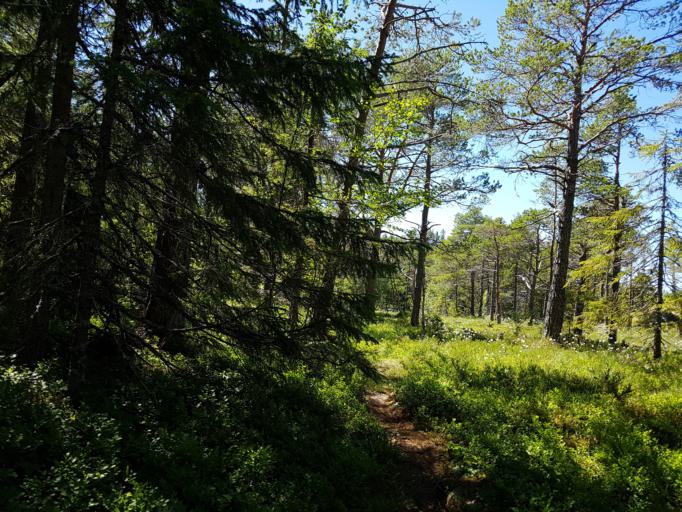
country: NO
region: Sor-Trondelag
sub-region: Melhus
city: Melhus
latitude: 63.4393
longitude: 10.2121
